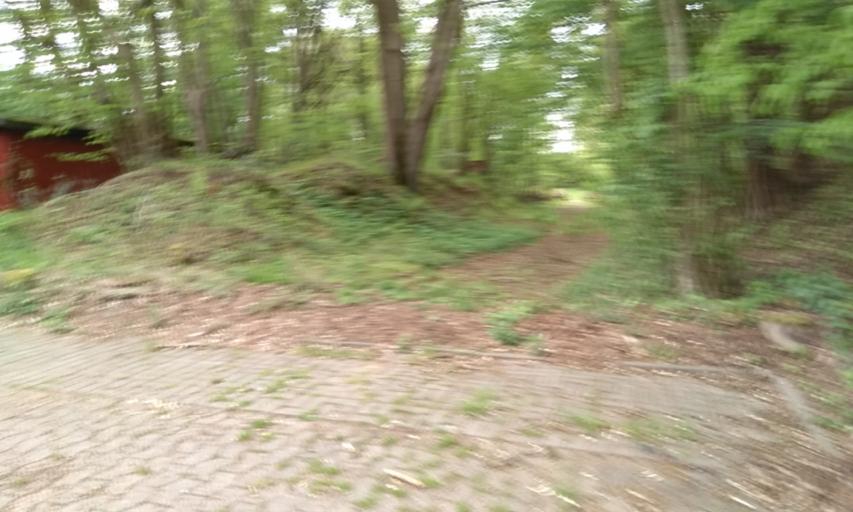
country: DE
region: Lower Saxony
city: Buxtehude
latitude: 53.4401
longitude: 9.6566
